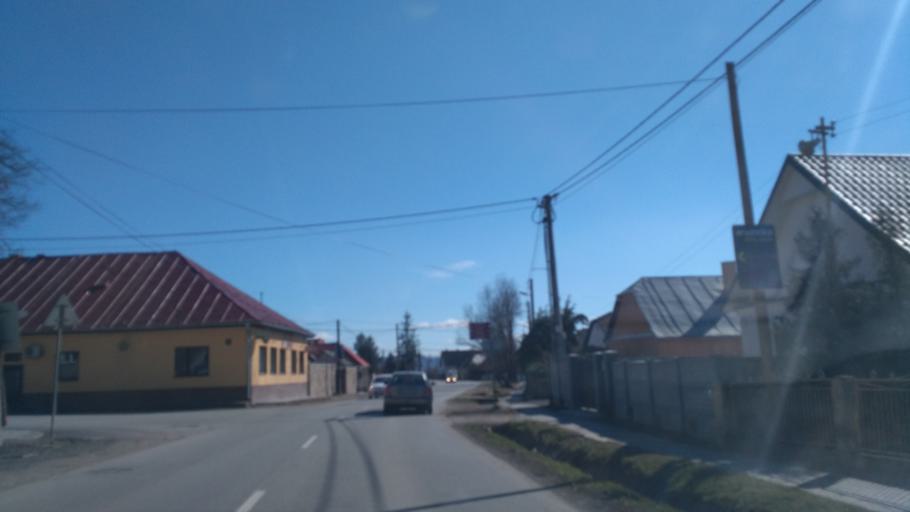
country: SK
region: Kosicky
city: Kosice
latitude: 48.6268
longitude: 21.3072
